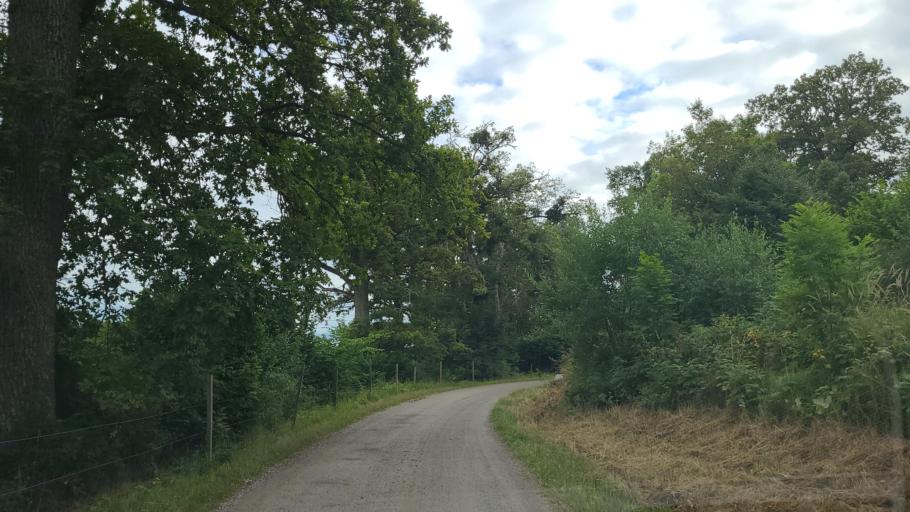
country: SE
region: Stockholm
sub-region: Upplands-Bro Kommun
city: Bro
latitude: 59.4616
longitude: 17.5855
